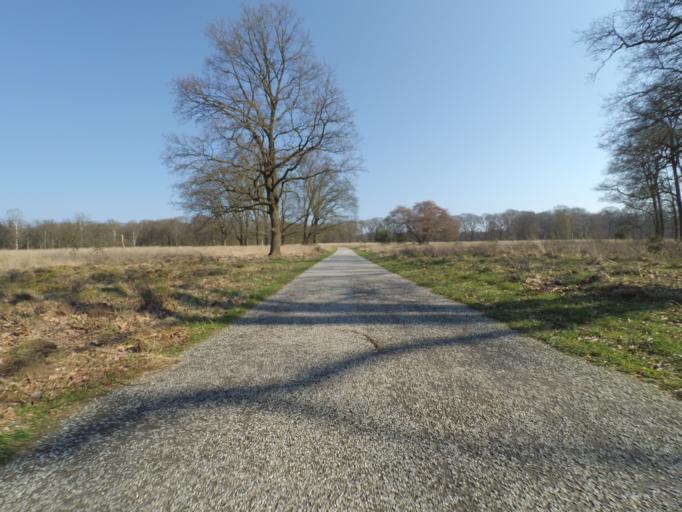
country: NL
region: Gelderland
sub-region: Gemeente Ede
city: Otterlo
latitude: 52.1101
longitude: 5.8418
